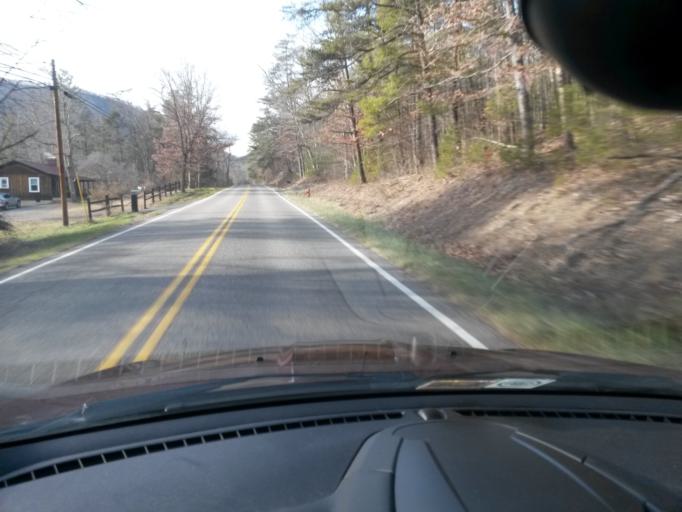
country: US
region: Virginia
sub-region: Rockbridge County
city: East Lexington
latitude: 37.9989
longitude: -79.5168
